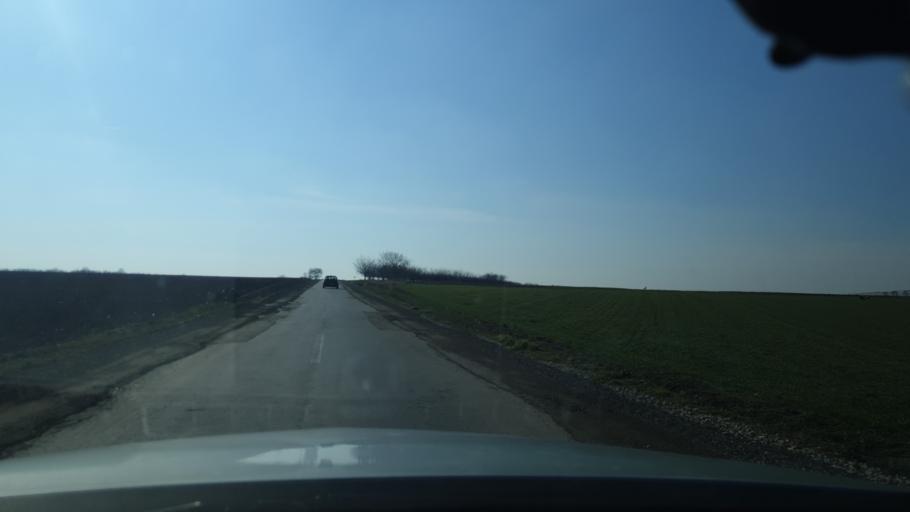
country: RS
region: Autonomna Pokrajina Vojvodina
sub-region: Sremski Okrug
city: Irig
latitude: 45.0830
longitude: 19.8487
